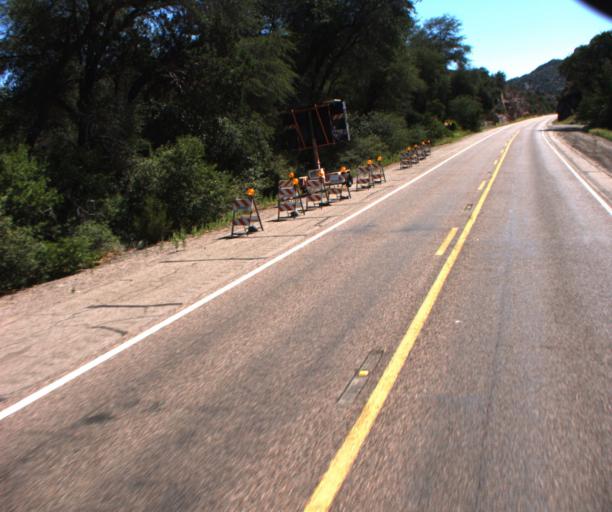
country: US
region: Arizona
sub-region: Pinal County
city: Superior
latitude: 33.3420
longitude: -111.0061
